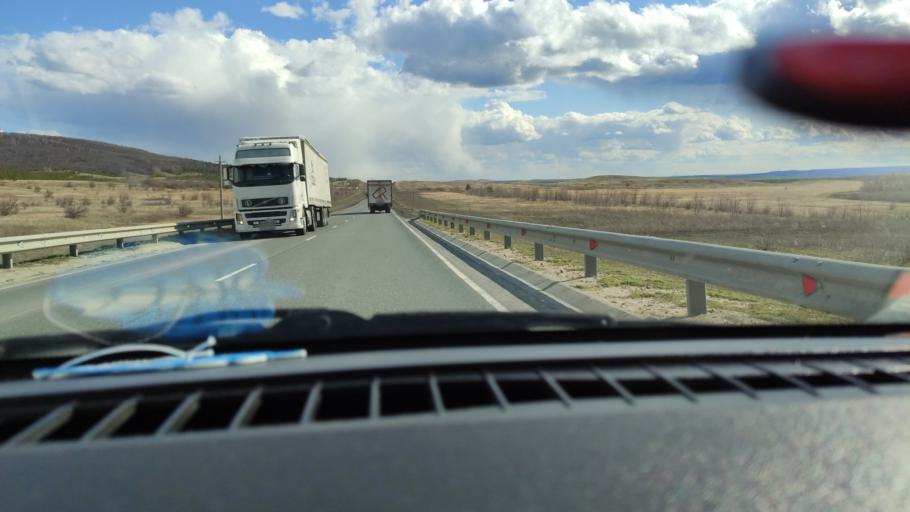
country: RU
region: Saratov
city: Alekseyevka
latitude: 52.3095
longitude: 47.9249
